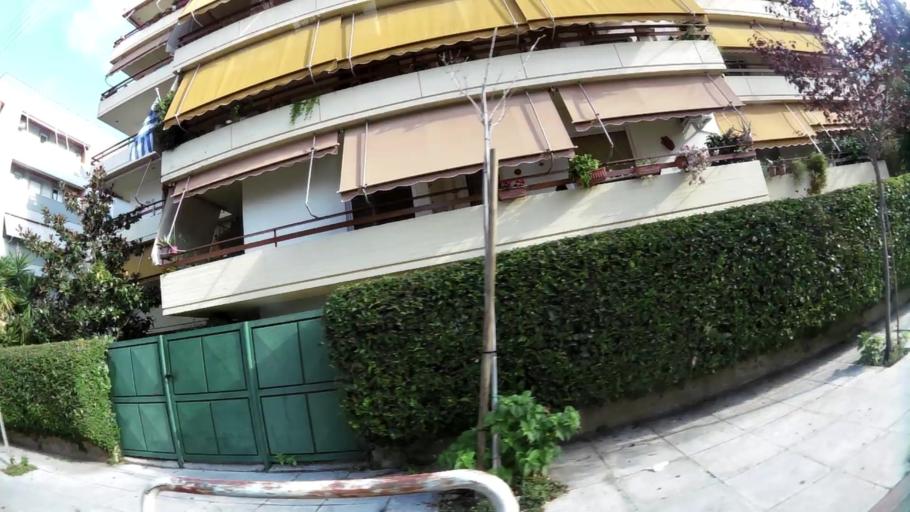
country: GR
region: Attica
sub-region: Nomarchia Athinas
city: Melissia
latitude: 38.0513
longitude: 23.8184
